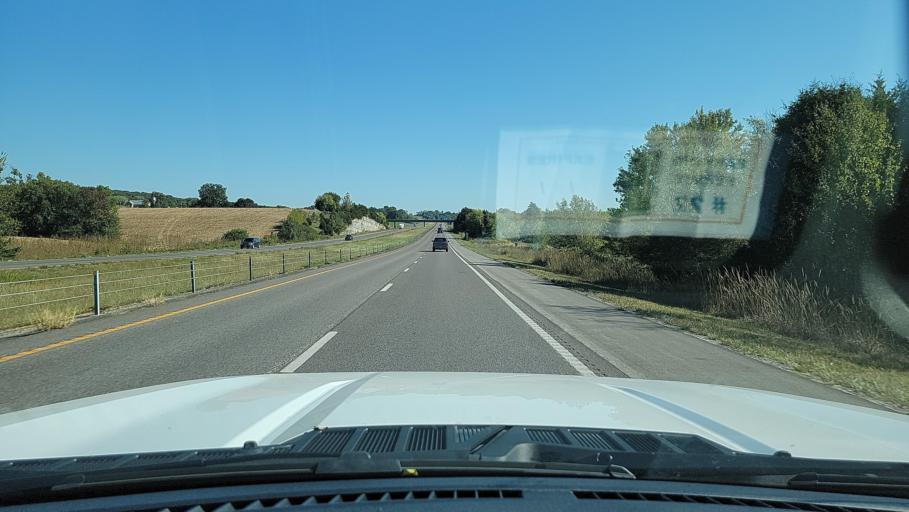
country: US
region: Missouri
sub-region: Sainte Genevieve County
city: Sainte Genevieve
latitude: 37.9528
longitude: -90.1520
